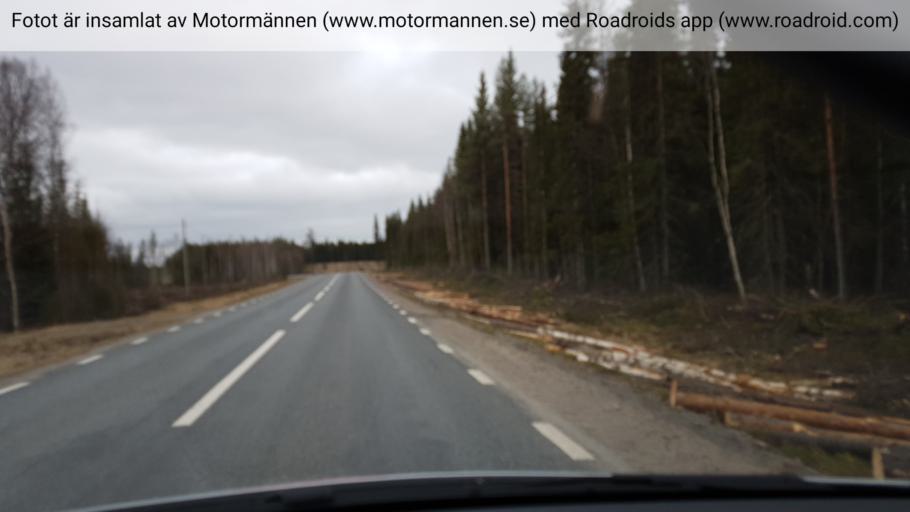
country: SE
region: Vaesternorrland
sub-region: OErnskoeldsviks Kommun
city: Bredbyn
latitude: 63.7359
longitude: 18.5002
